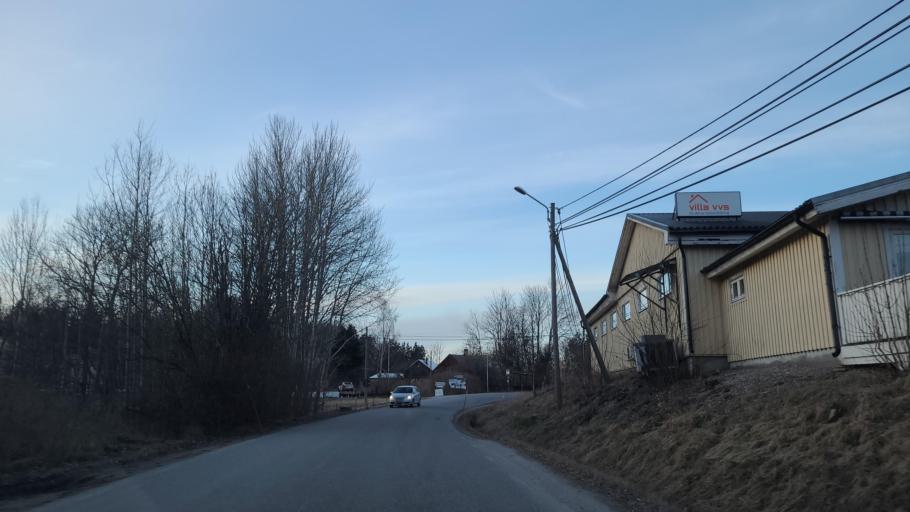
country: SE
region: Stockholm
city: Stenhamra
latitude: 59.4029
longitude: 17.6567
